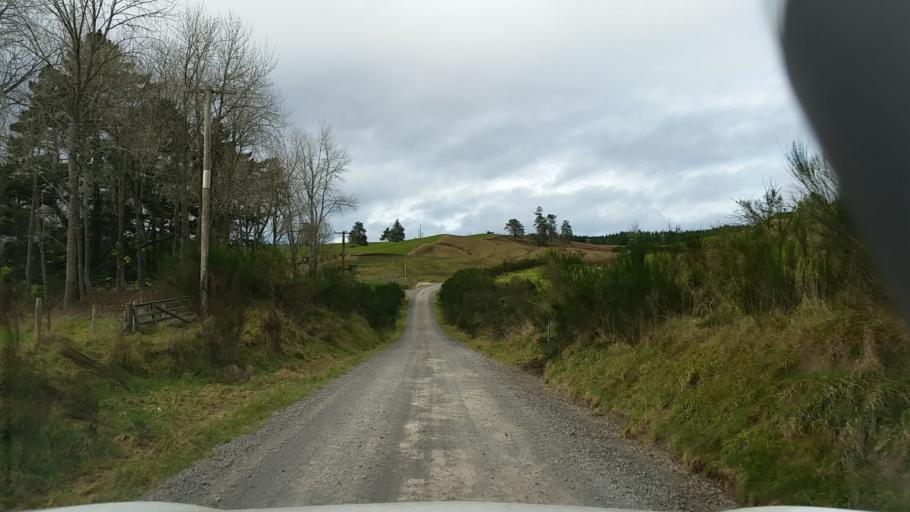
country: NZ
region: Bay of Plenty
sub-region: Whakatane District
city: Murupara
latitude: -38.3368
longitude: 176.5375
